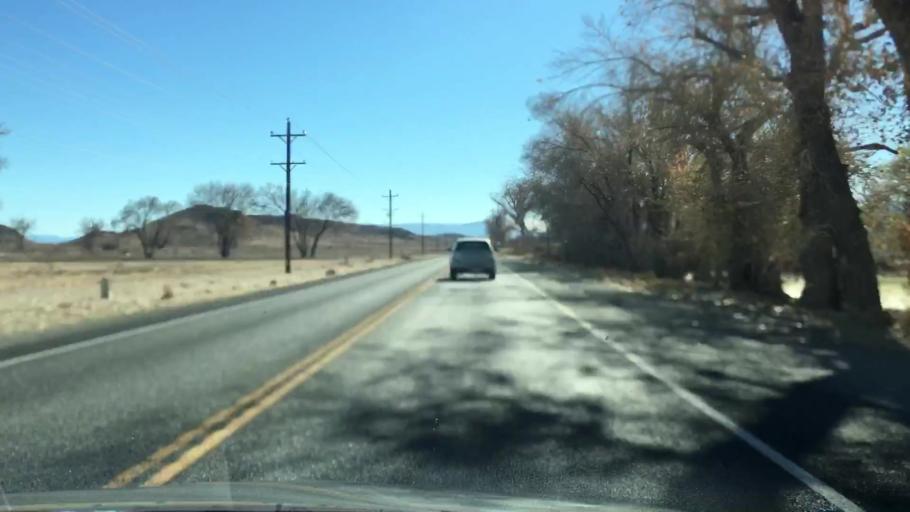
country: US
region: Nevada
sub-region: Lyon County
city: Yerington
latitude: 39.0317
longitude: -119.1816
